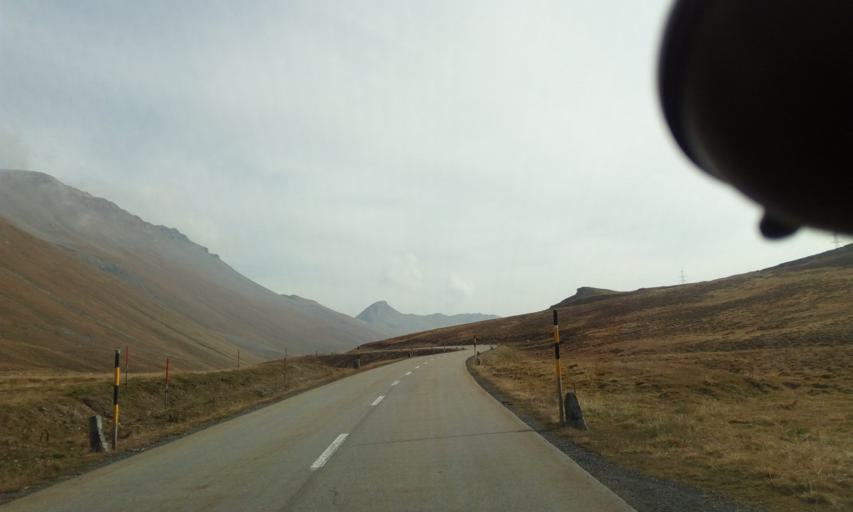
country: CH
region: Grisons
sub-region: Maloja District
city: Samedan
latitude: 46.5855
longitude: 9.8522
